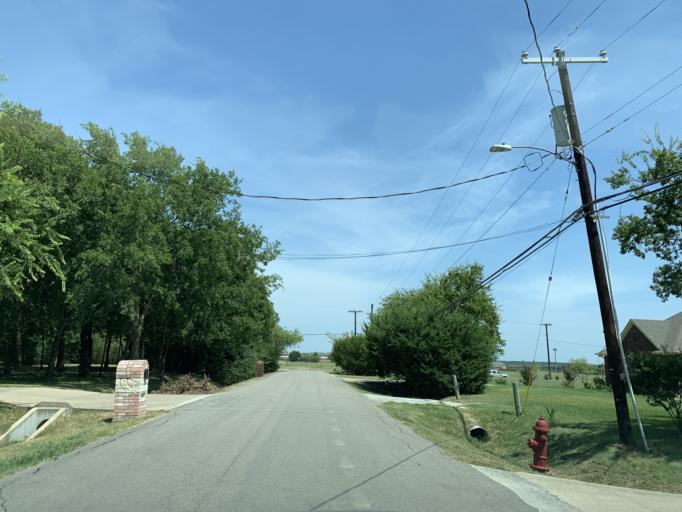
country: US
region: Texas
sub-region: Dallas County
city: Cedar Hill
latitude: 32.6474
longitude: -97.0156
